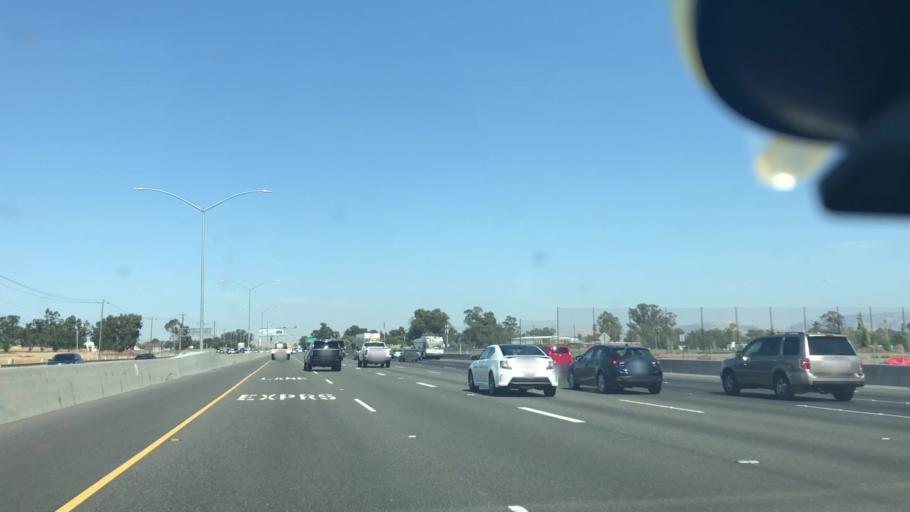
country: US
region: California
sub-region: Alameda County
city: Pleasanton
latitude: 37.7010
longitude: -121.8397
